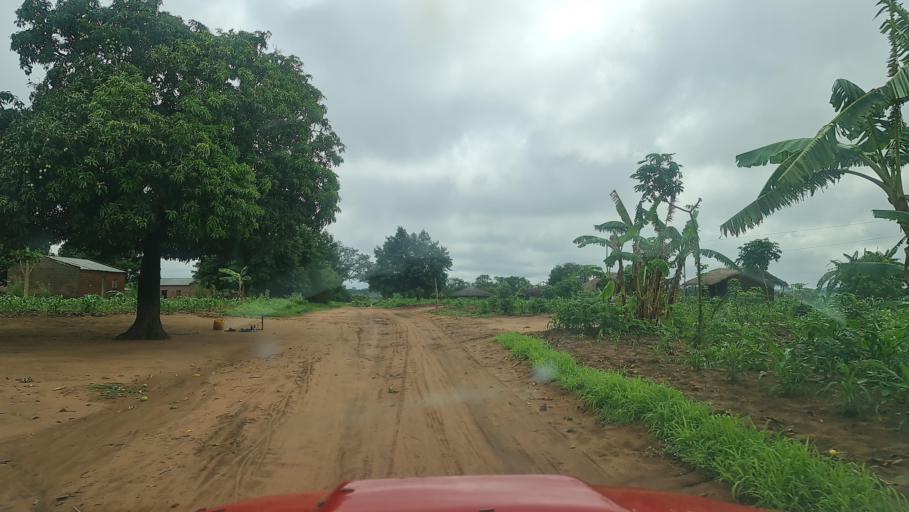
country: MW
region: Southern Region
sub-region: Nsanje District
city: Nsanje
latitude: -17.2042
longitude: 35.6842
